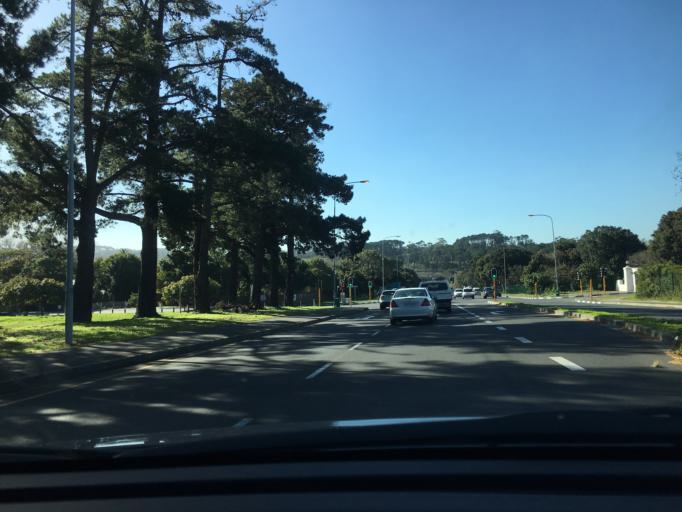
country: ZA
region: Western Cape
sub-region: City of Cape Town
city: Bergvliet
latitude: -34.0174
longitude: 18.4495
